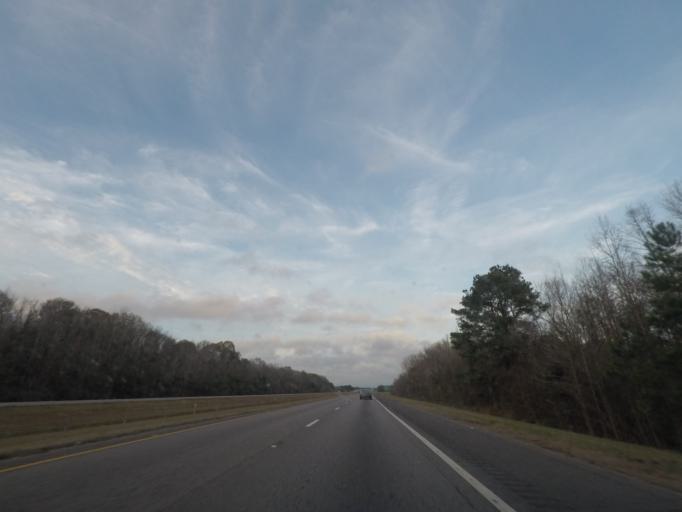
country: US
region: South Carolina
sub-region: Orangeburg County
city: Holly Hill
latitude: 33.3741
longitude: -80.5220
